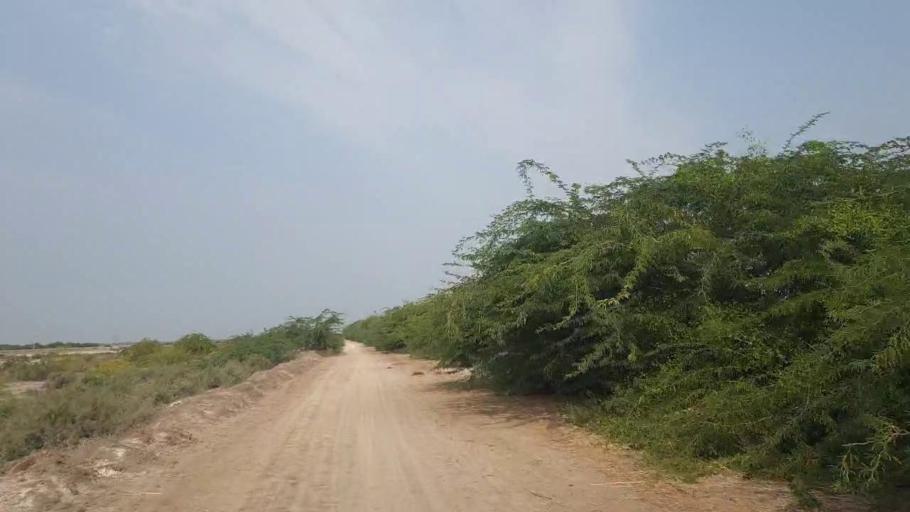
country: PK
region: Sindh
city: Badin
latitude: 24.5579
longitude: 68.7321
